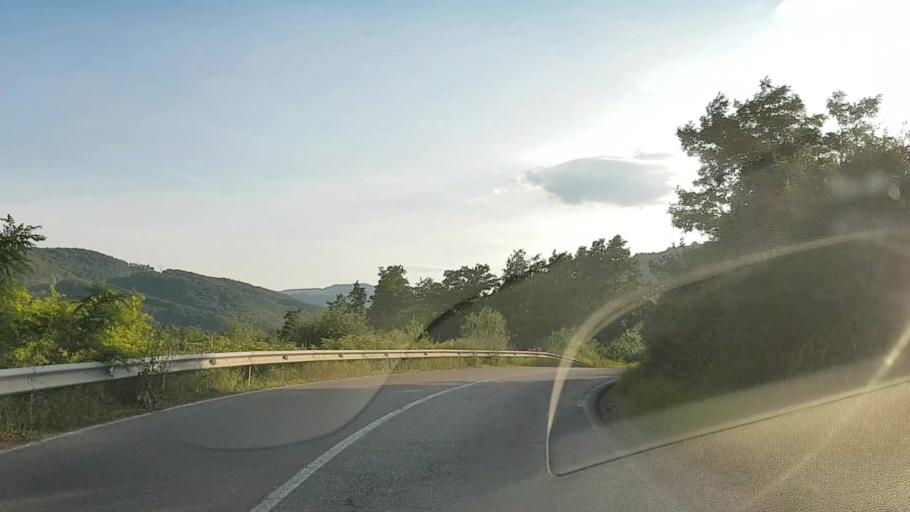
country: RO
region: Harghita
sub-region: Comuna Praid
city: Praid
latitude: 46.5688
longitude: 25.1687
